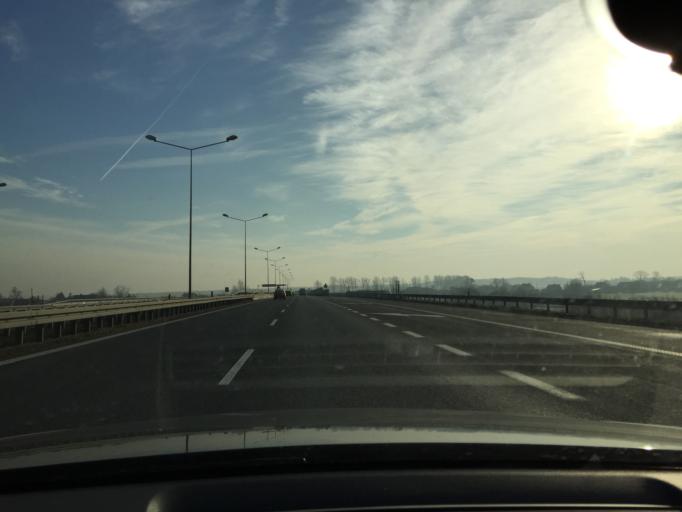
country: PL
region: Silesian Voivodeship
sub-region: Powiat gliwicki
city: Sosnicowice
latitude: 50.2792
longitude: 18.5718
